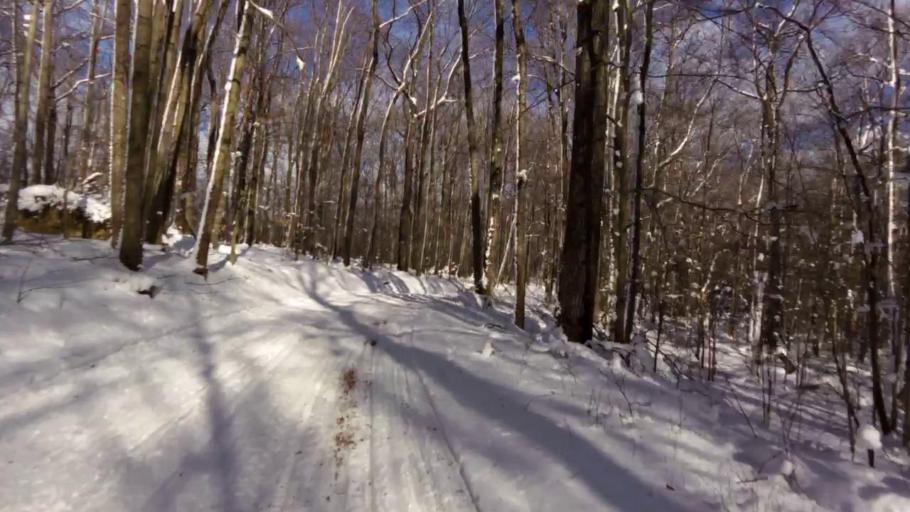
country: US
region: New York
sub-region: Cattaraugus County
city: Salamanca
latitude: 42.0703
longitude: -78.6948
